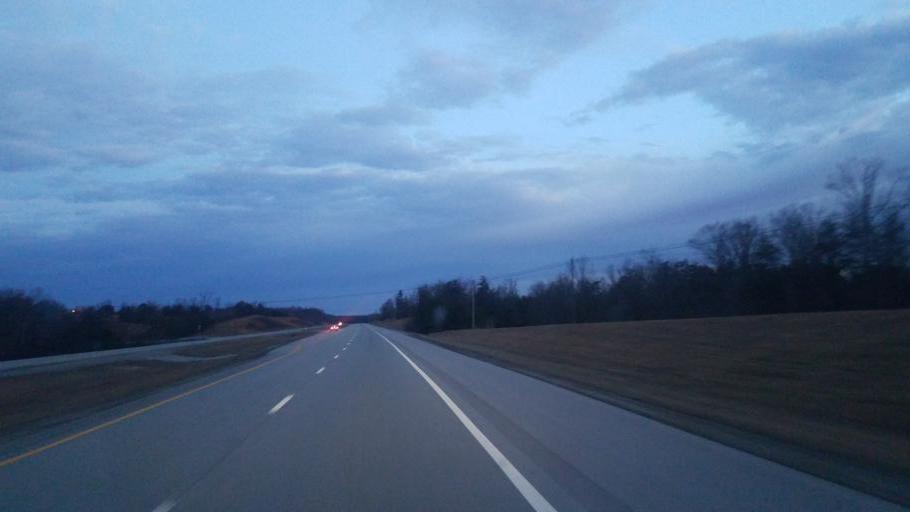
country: US
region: Tennessee
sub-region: Van Buren County
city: Spencer
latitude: 35.6775
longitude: -85.4752
